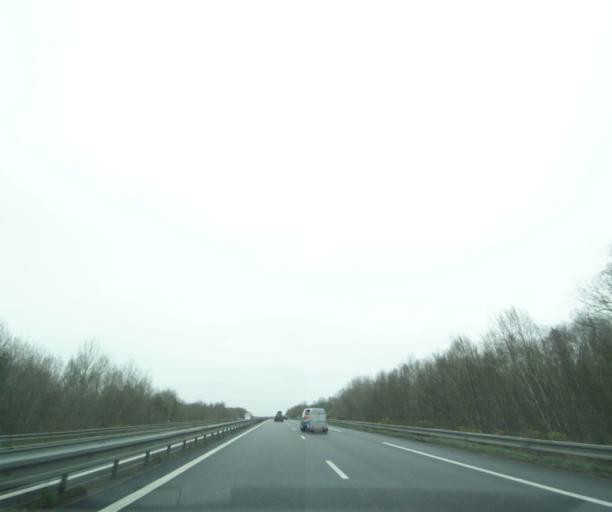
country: FR
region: Centre
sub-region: Departement du Loir-et-Cher
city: Salbris
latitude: 47.4372
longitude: 2.0104
